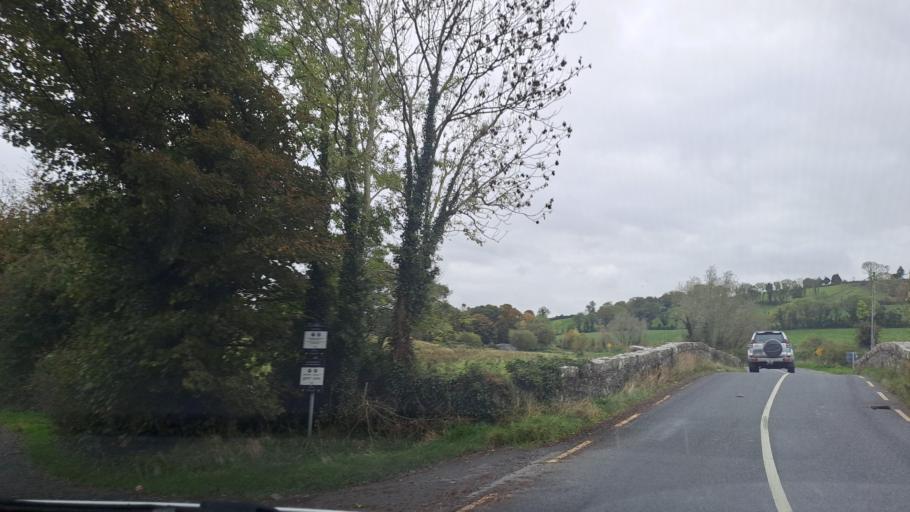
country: IE
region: Ulster
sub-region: An Cabhan
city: Cootehill
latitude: 54.0434
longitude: -7.0477
